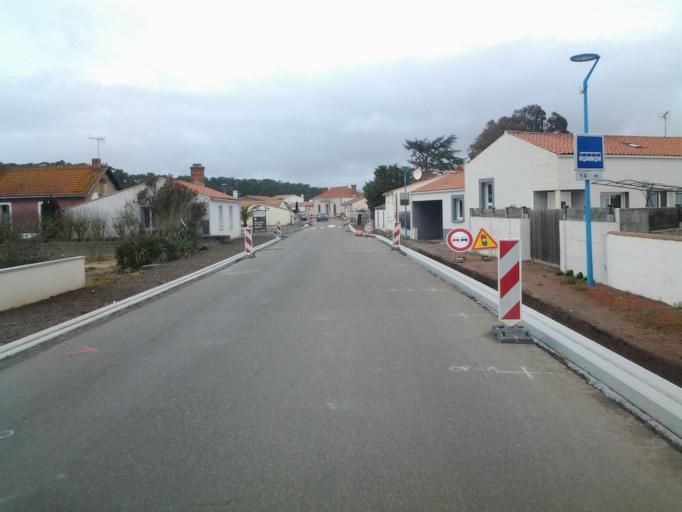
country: FR
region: Pays de la Loire
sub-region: Departement de la Vendee
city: Longeville-sur-Mer
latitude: 46.3867
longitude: -1.4685
